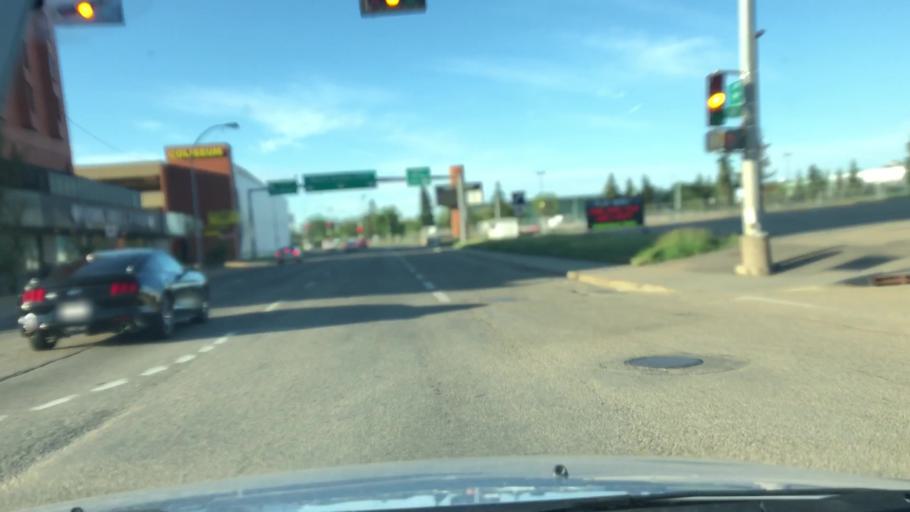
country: CA
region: Alberta
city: Edmonton
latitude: 53.5720
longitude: -113.4537
